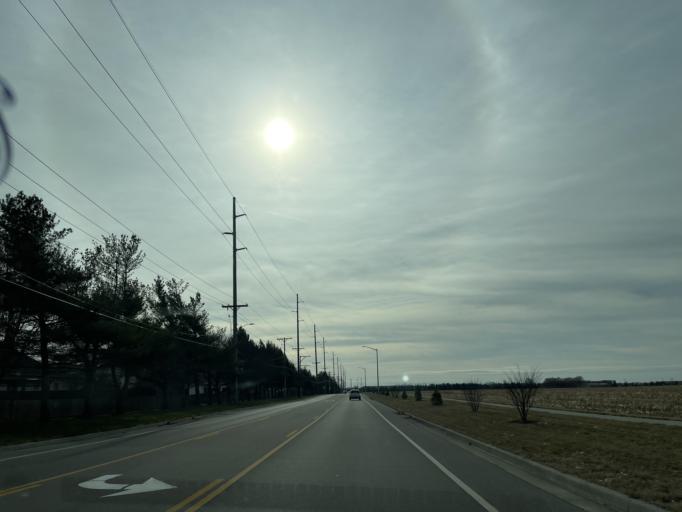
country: US
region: Illinois
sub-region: Sangamon County
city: Jerome
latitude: 39.7666
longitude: -89.7346
